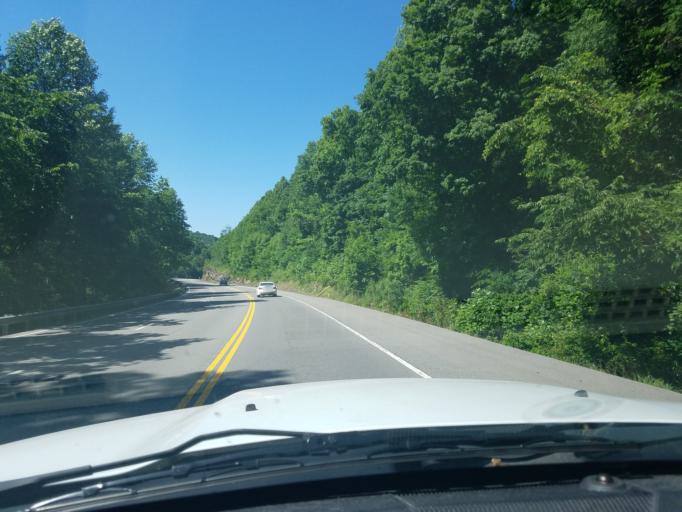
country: US
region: Tennessee
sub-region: Sumner County
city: Westmoreland
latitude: 36.5396
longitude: -86.2433
